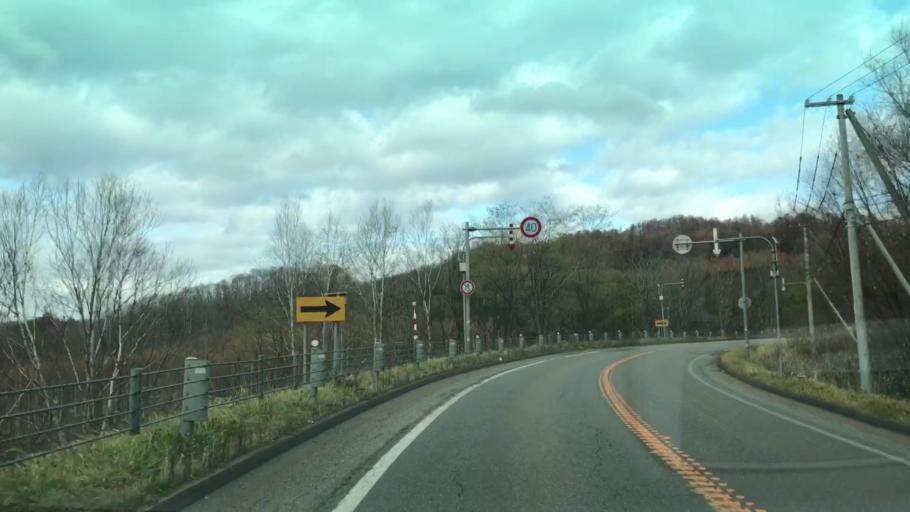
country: JP
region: Hokkaido
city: Shimo-furano
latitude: 42.8864
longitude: 142.4337
